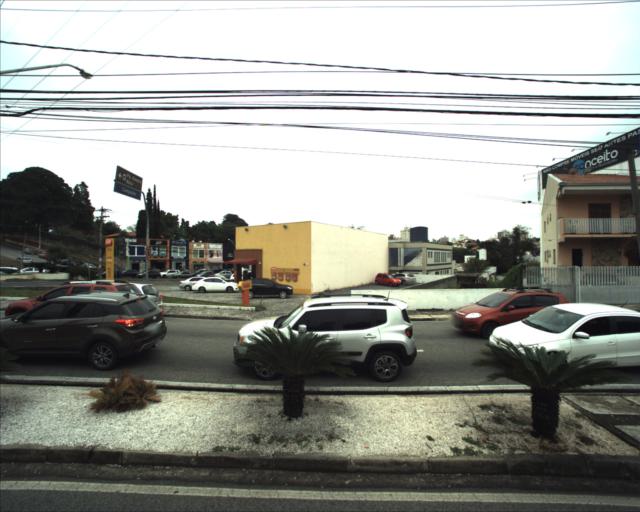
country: BR
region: Sao Paulo
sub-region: Sorocaba
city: Sorocaba
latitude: -23.5157
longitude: -47.4653
